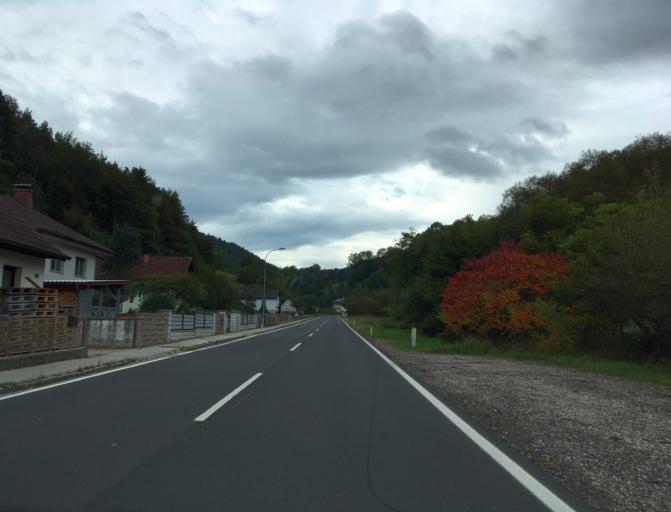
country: AT
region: Lower Austria
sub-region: Politischer Bezirk Neunkirchen
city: Edlitz
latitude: 47.5872
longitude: 16.1466
